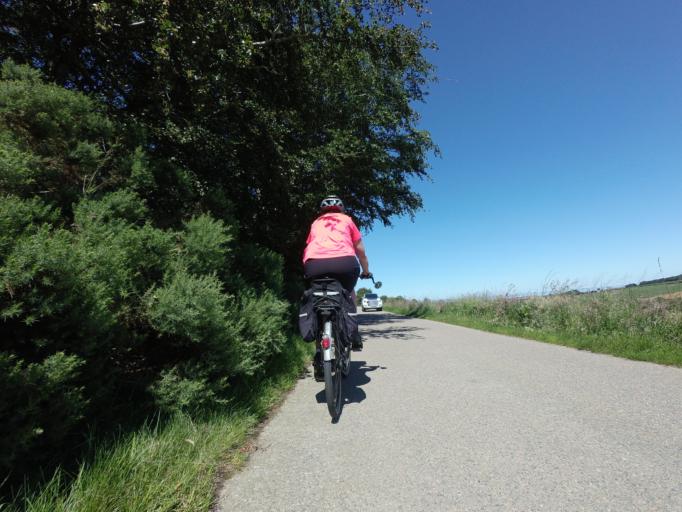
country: GB
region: Scotland
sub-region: Aberdeenshire
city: Macduff
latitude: 57.6481
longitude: -2.5044
